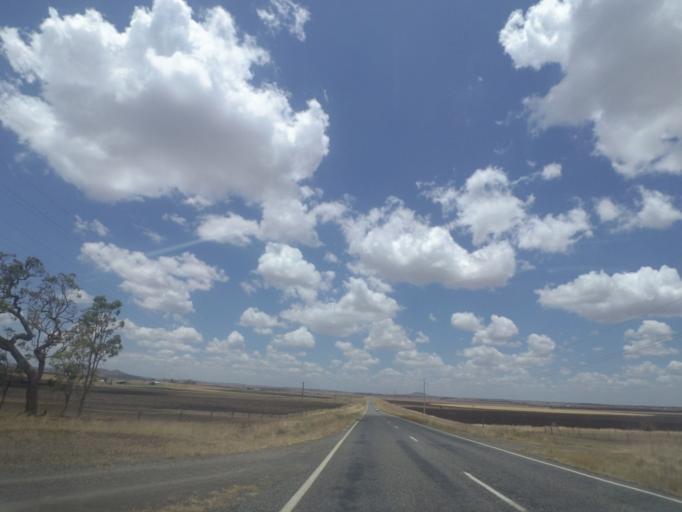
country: AU
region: Queensland
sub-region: Toowoomba
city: Top Camp
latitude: -27.8936
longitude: 151.9739
